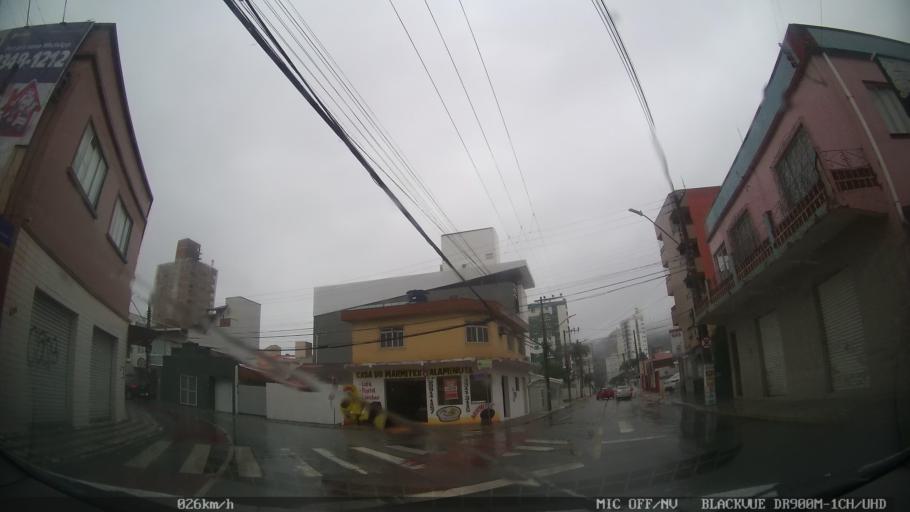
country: BR
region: Santa Catarina
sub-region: Itajai
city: Itajai
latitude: -26.9100
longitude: -48.6690
